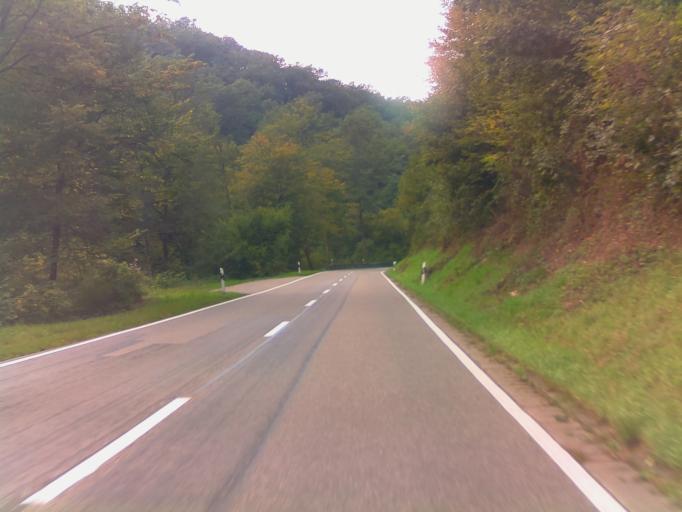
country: DE
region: Hesse
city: Hirschhorn
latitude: 49.4605
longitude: 8.8693
